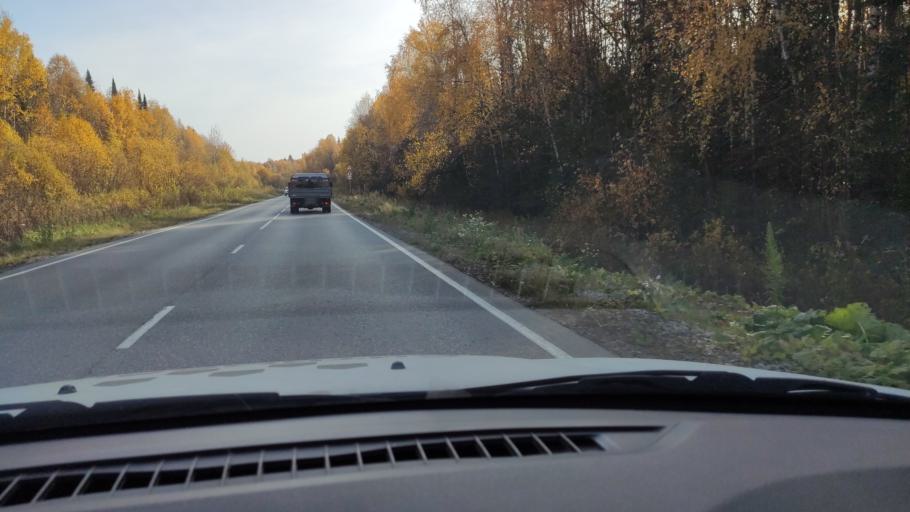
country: RU
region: Perm
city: Novyye Lyady
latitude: 58.0226
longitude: 56.6426
